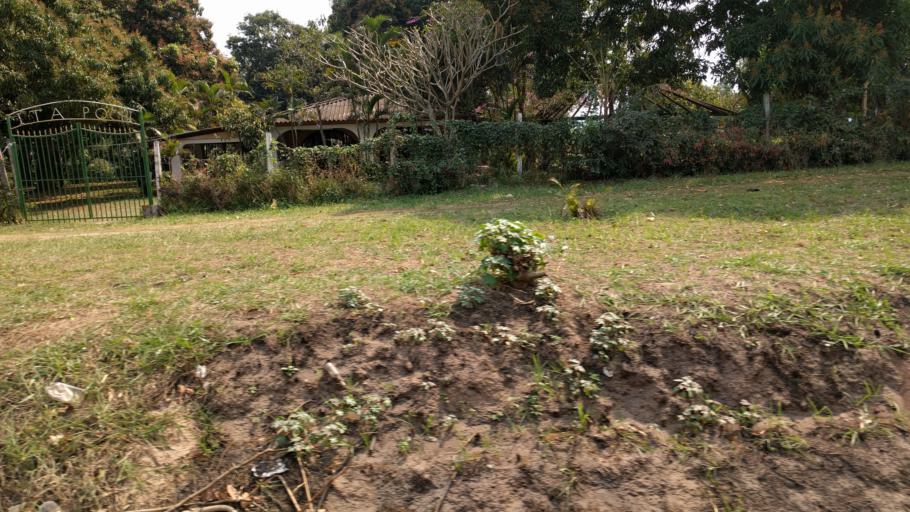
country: BO
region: Santa Cruz
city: Santa Rita
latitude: -17.9092
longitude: -63.3416
